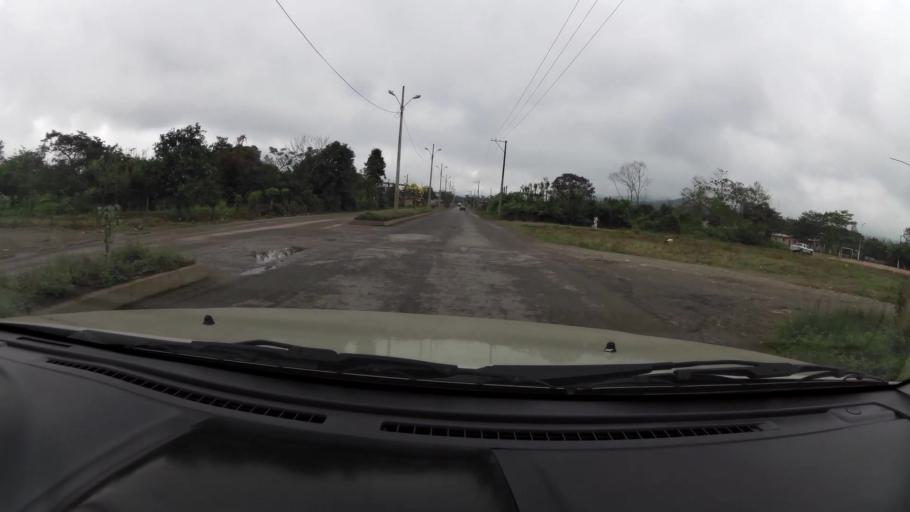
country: EC
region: El Oro
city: Pasaje
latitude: -3.3420
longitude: -79.7999
